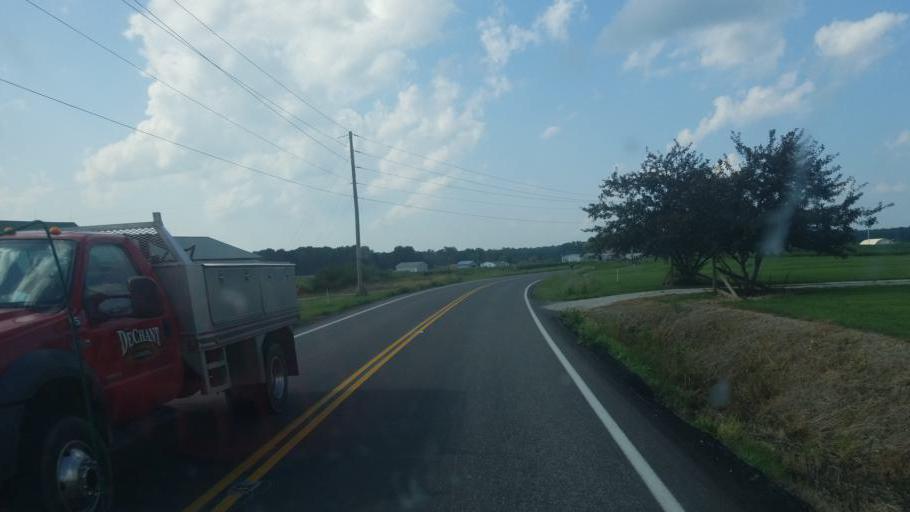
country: US
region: Ohio
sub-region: Wayne County
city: West Salem
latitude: 40.9608
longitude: -82.0857
